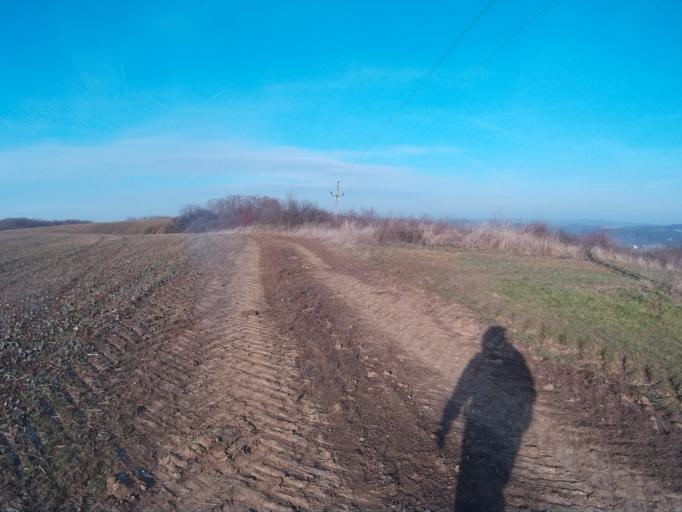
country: HU
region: Nograd
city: Bercel
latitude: 47.9335
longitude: 19.4301
